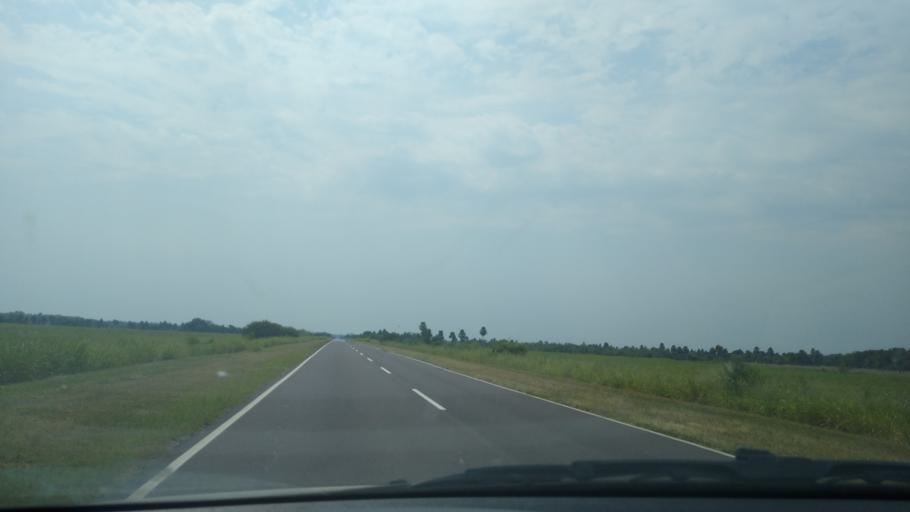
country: AR
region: Chaco
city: La Eduvigis
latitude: -27.0011
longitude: -58.9724
